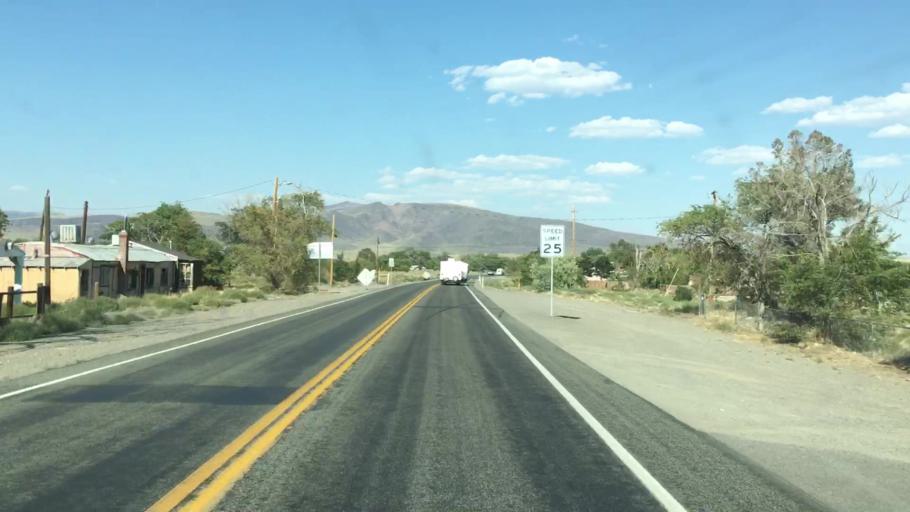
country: US
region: Nevada
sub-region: Lyon County
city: Fernley
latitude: 39.6308
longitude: -119.2899
